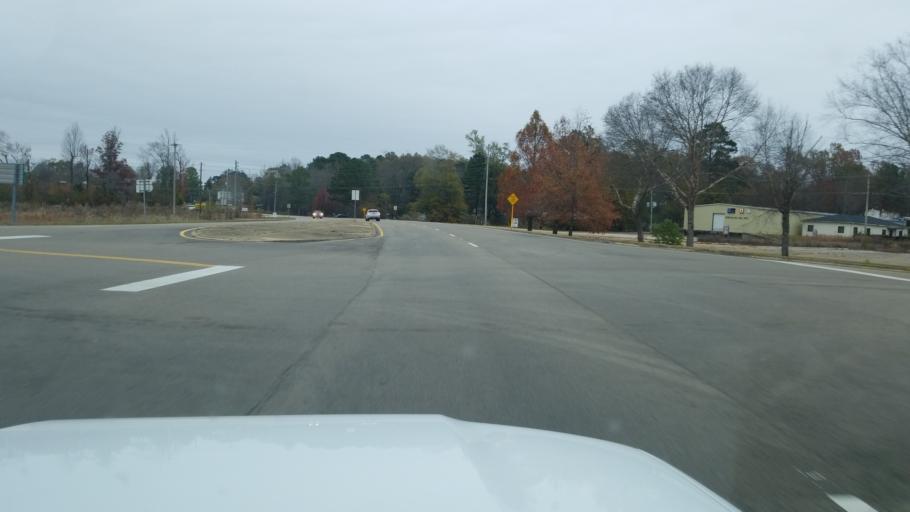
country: US
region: Mississippi
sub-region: Lee County
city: Tupelo
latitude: 34.2885
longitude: -88.6765
